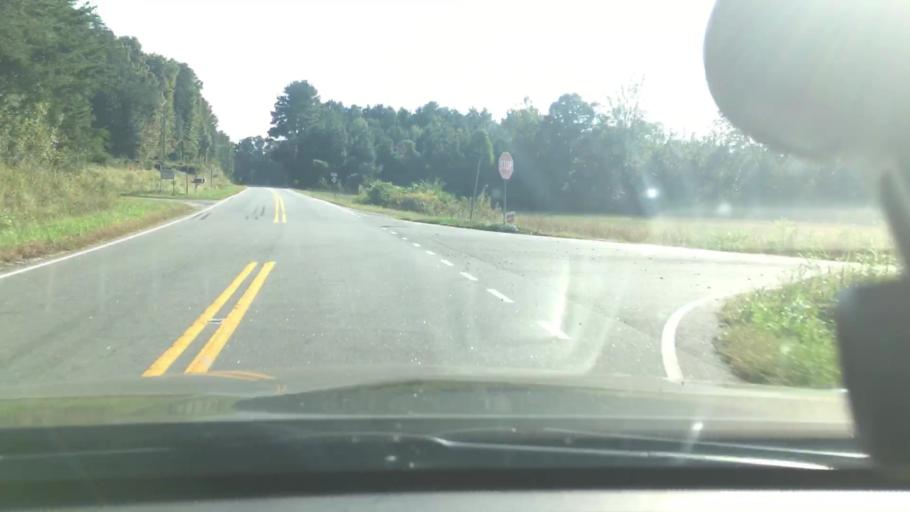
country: US
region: North Carolina
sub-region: Rutherford County
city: Rutherfordton
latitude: 35.3583
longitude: -81.9847
